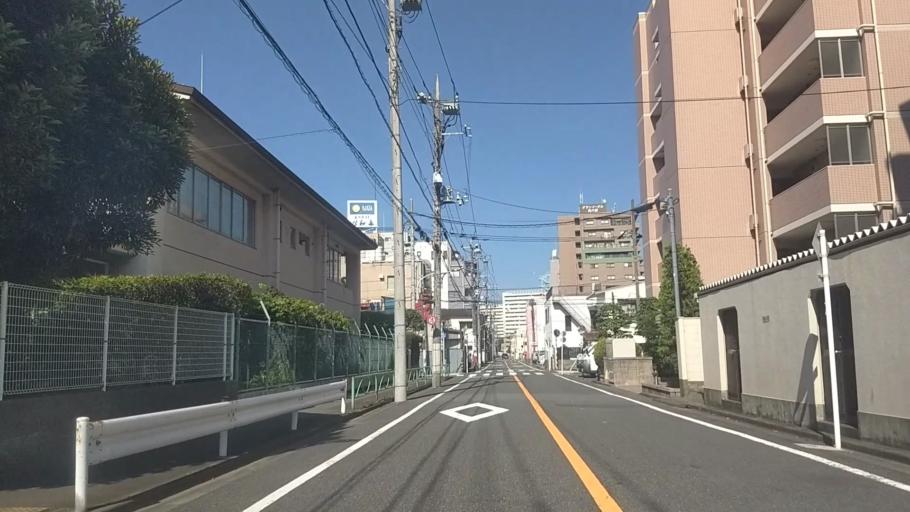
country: JP
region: Kanagawa
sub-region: Kawasaki-shi
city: Kawasaki
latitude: 35.5428
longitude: 139.7162
